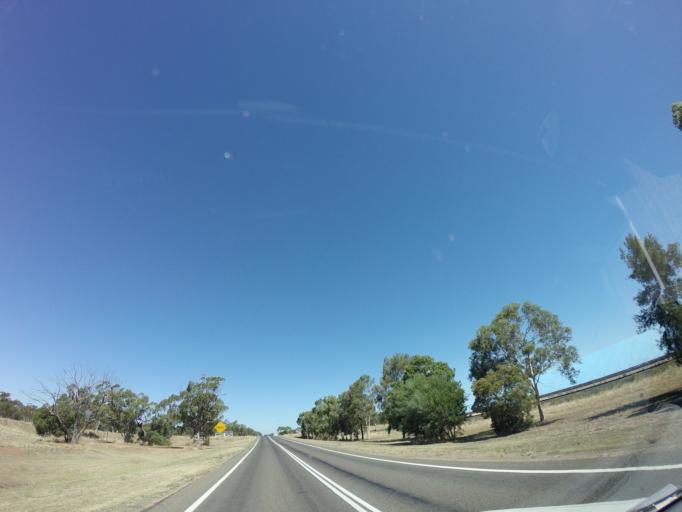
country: AU
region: New South Wales
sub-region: Bogan
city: Nyngan
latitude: -31.5690
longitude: 147.2098
